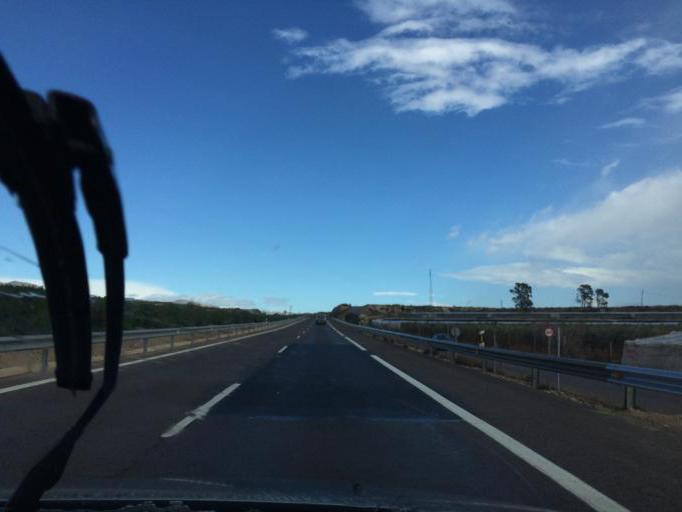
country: ES
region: Andalusia
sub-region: Provincia de Almeria
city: Nijar
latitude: 36.8871
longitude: -2.2153
